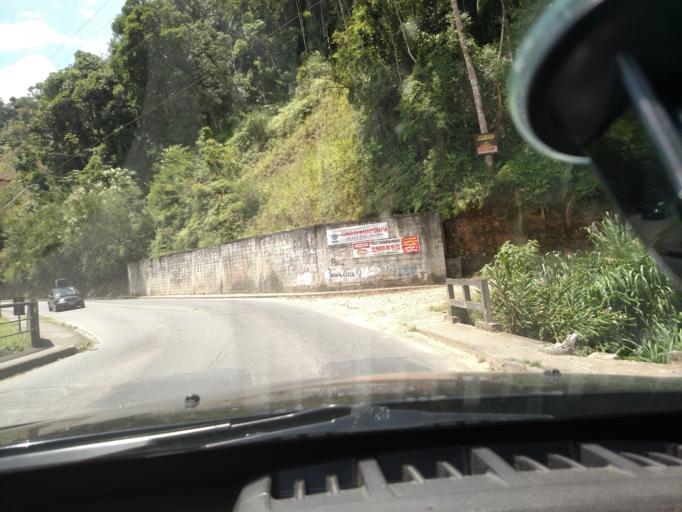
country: BR
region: Santa Catarina
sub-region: Blumenau
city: Blumenau
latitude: -26.9808
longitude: -49.0750
